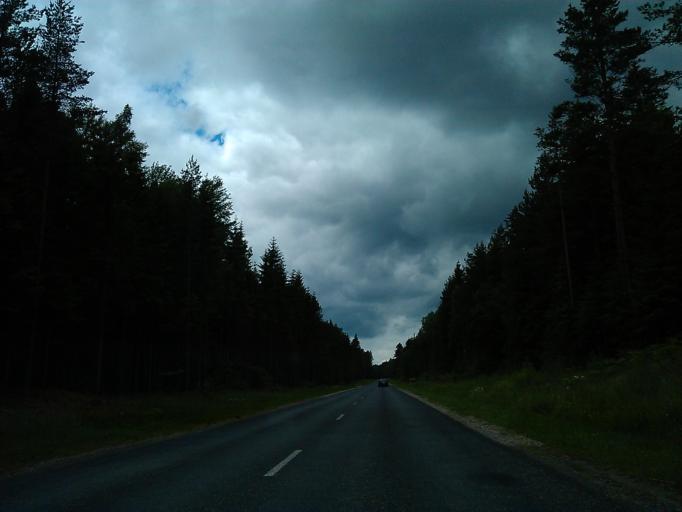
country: LV
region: Talsu Rajons
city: Stende
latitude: 57.0894
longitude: 22.4013
